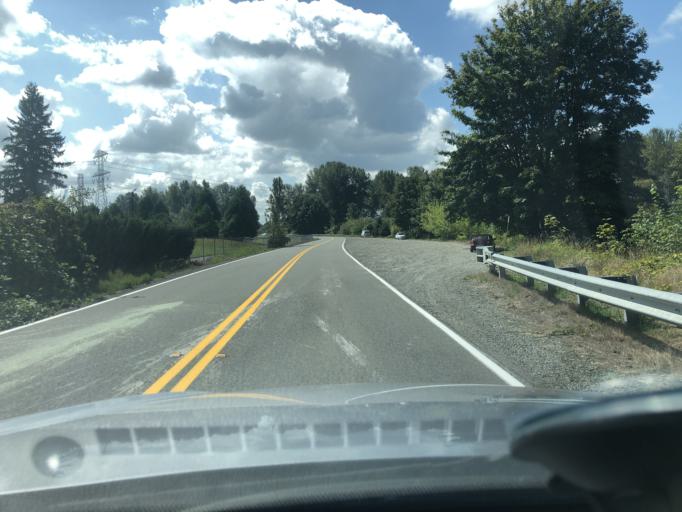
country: US
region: Washington
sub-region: King County
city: Lea Hill
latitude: 47.3404
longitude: -122.2065
